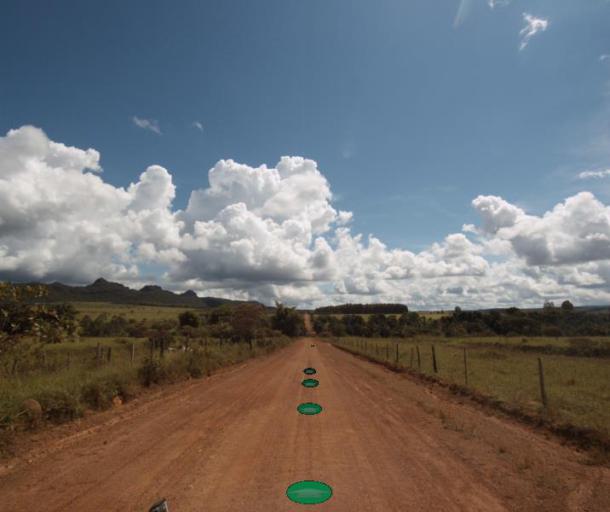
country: BR
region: Goias
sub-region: Pirenopolis
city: Pirenopolis
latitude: -15.7813
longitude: -48.8136
